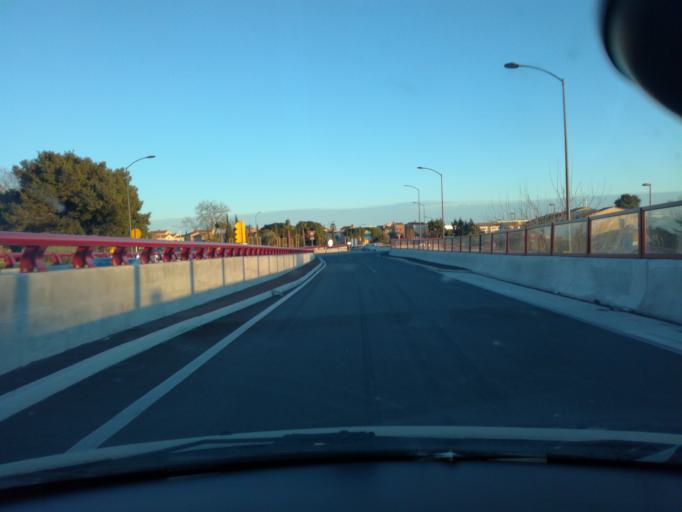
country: FR
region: Provence-Alpes-Cote d'Azur
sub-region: Departement du Var
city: Puget-sur-Argens
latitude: 43.4562
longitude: 6.6887
